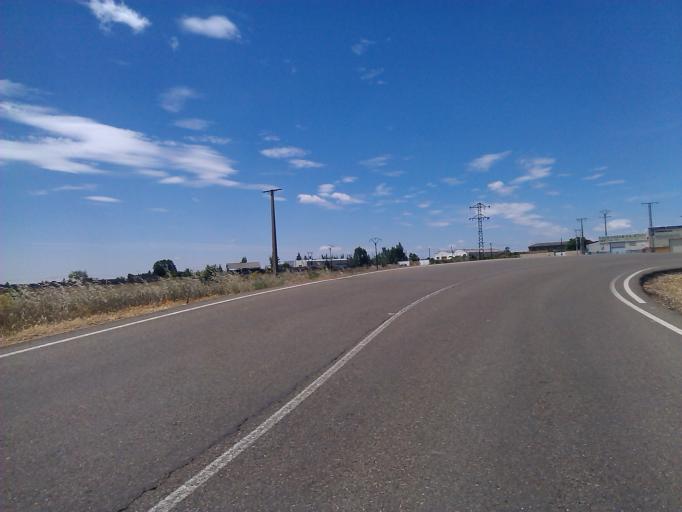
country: ES
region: Castille and Leon
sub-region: Provincia de Leon
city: Valverde de la Virgen
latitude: 42.5772
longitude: -5.6483
